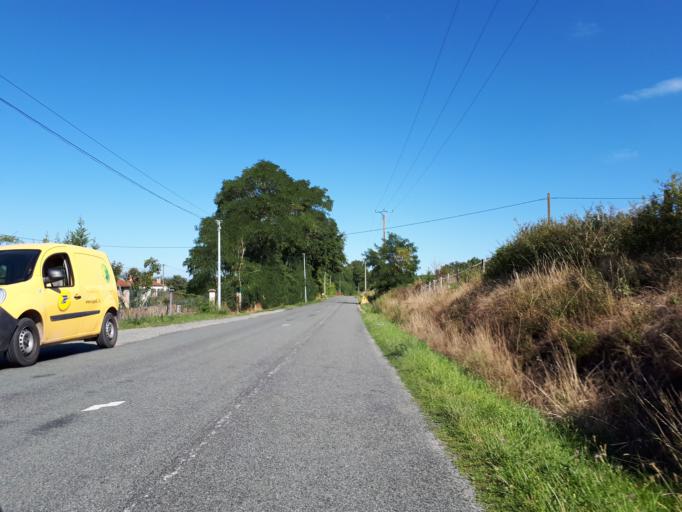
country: FR
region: Rhone-Alpes
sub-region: Departement de la Loire
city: Civens
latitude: 45.7685
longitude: 4.2618
